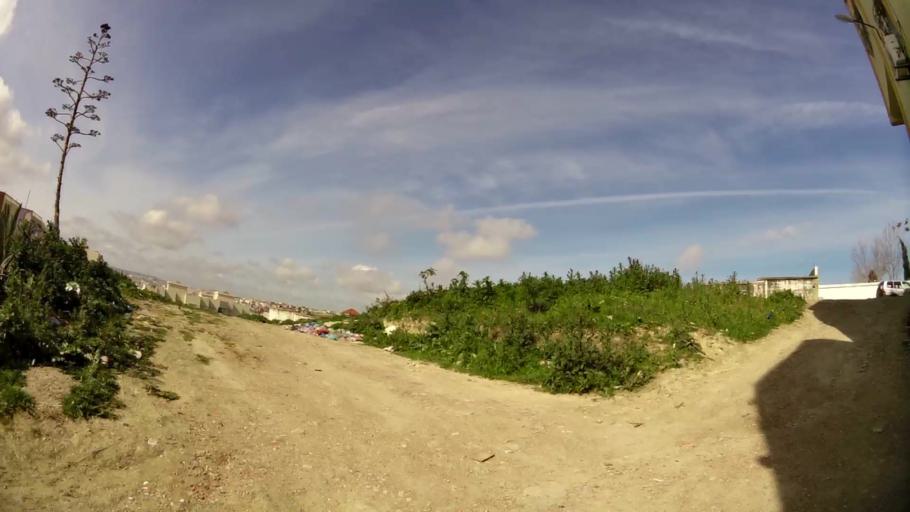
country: MA
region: Tanger-Tetouan
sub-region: Tanger-Assilah
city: Tangier
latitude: 35.7685
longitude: -5.7735
